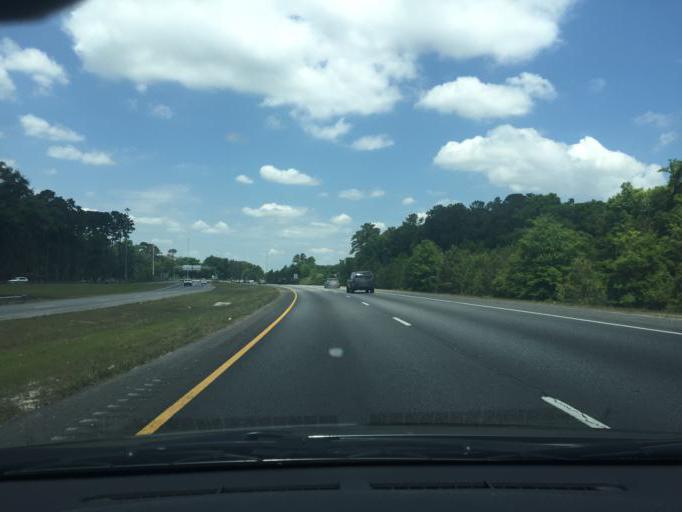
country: US
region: Georgia
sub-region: Chatham County
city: Isle of Hope
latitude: 32.0068
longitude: -81.0790
